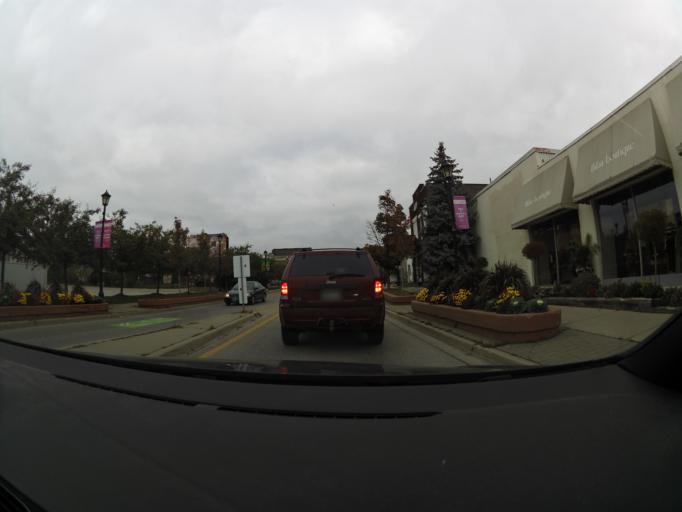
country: CA
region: Ontario
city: Kitchener
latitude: 43.4468
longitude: -80.4822
